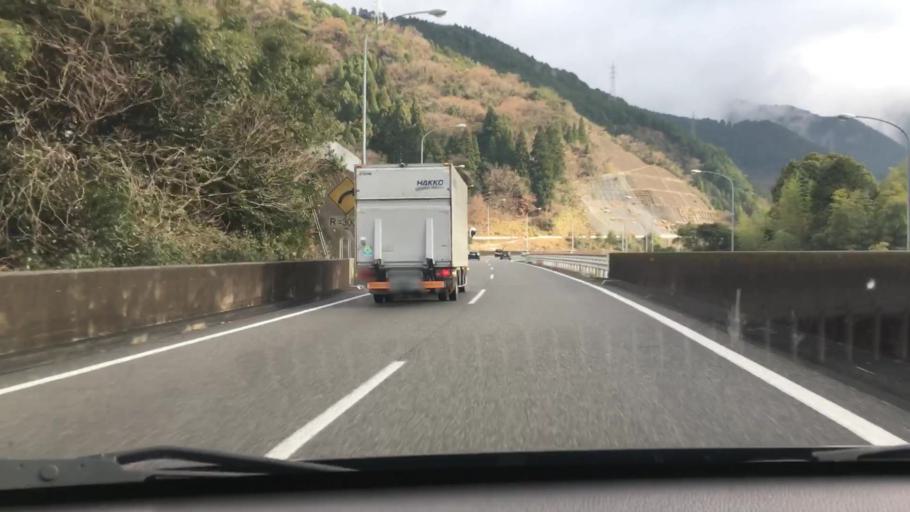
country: JP
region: Kumamoto
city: Yatsushiro
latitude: 32.4008
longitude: 130.6999
